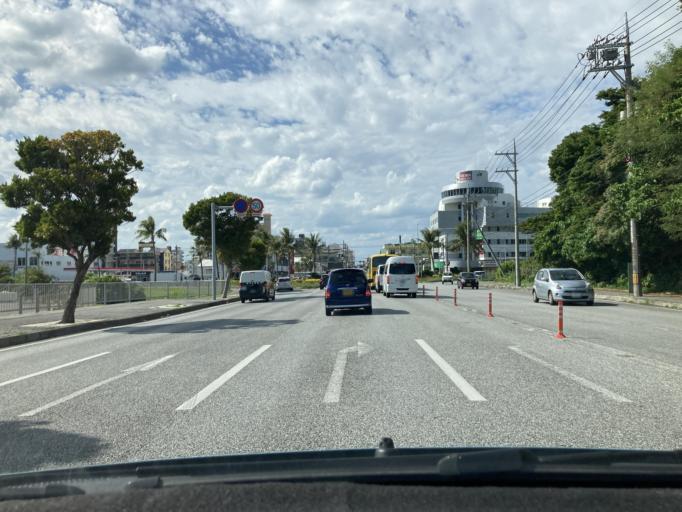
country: JP
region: Okinawa
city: Chatan
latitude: 26.3082
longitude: 127.7653
